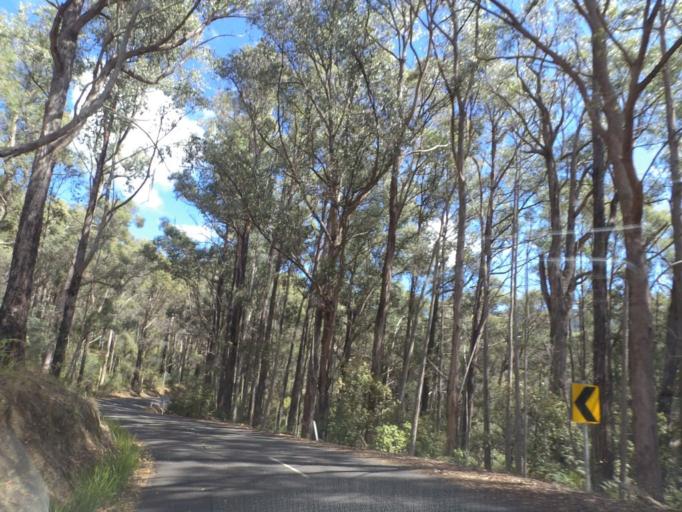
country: AU
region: Victoria
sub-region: Murrindindi
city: Alexandra
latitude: -37.3286
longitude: 145.9394
